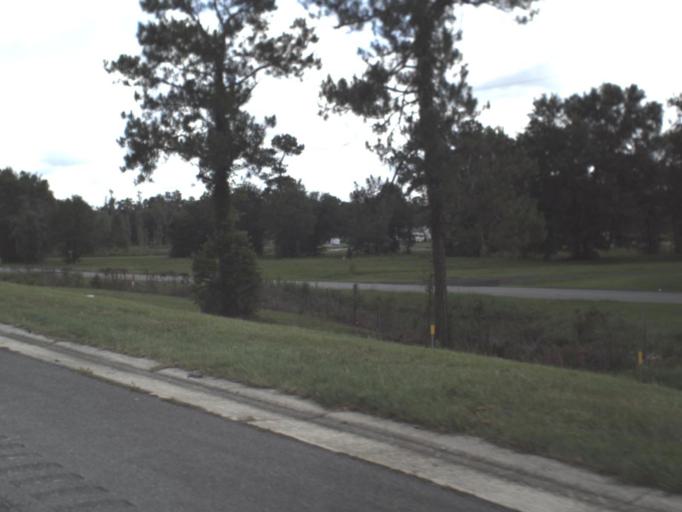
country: US
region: Florida
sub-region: Columbia County
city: Lake City
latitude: 30.1437
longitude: -82.6700
